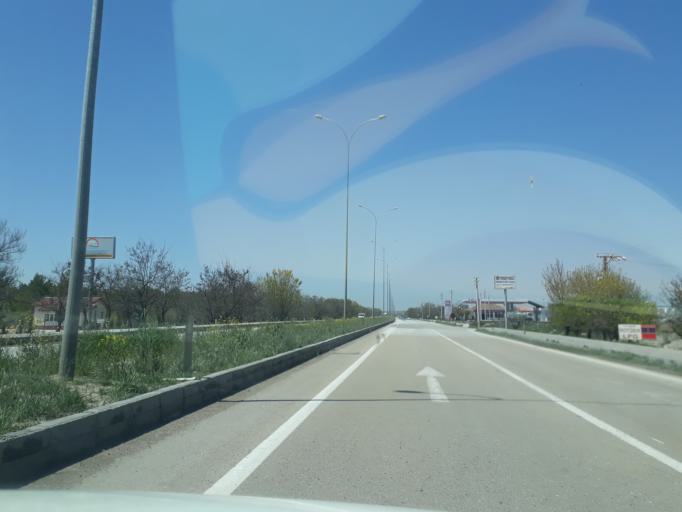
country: TR
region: Konya
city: Karapinar
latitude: 37.7140
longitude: 33.5271
